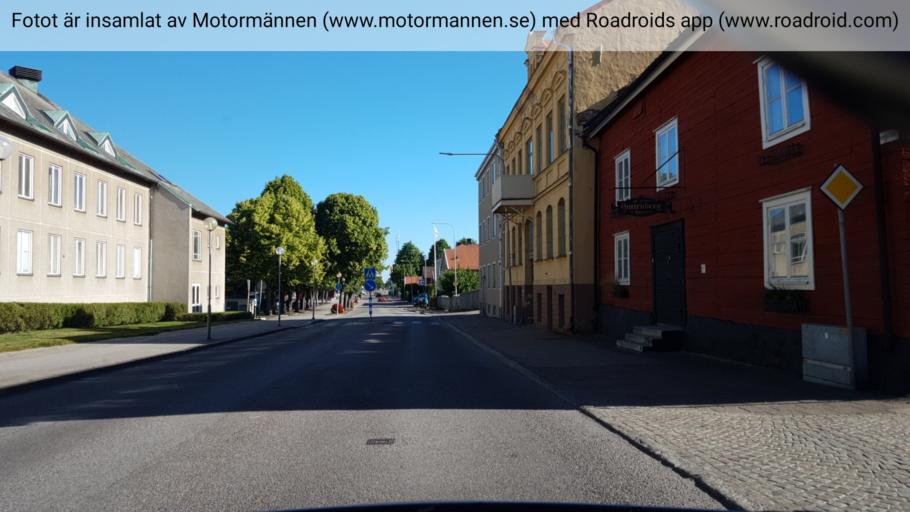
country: SE
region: Vaestra Goetaland
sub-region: Mariestads Kommun
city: Mariestad
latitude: 58.7100
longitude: 13.8198
